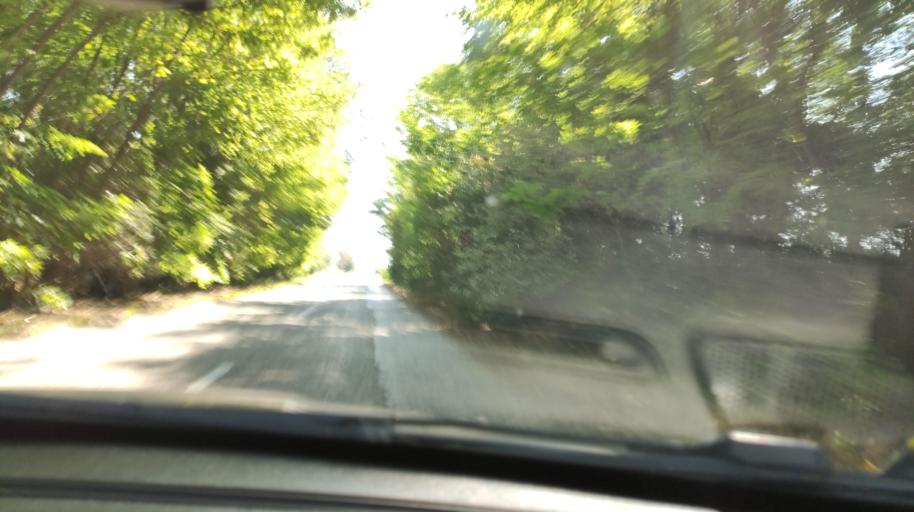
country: RS
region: Autonomna Pokrajina Vojvodina
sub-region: Severnobacki Okrug
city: Backa Topola
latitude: 45.8669
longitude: 19.6158
